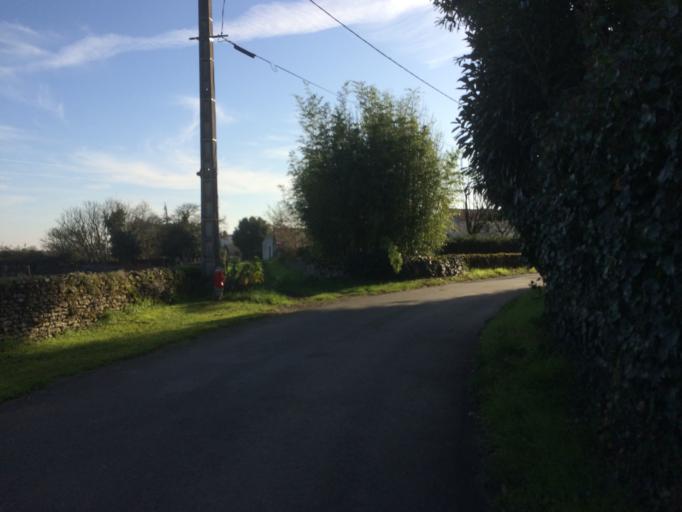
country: FR
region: Pays de la Loire
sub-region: Departement de la Vendee
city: Chaille-les-Marais
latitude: 46.3759
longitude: -1.0156
